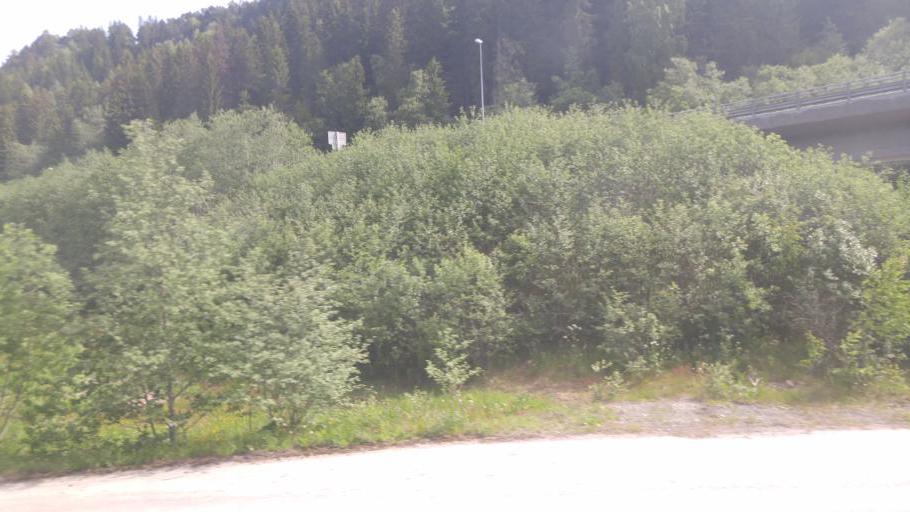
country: NO
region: Sor-Trondelag
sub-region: Midtre Gauldal
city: Storen
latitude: 63.0384
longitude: 10.2971
